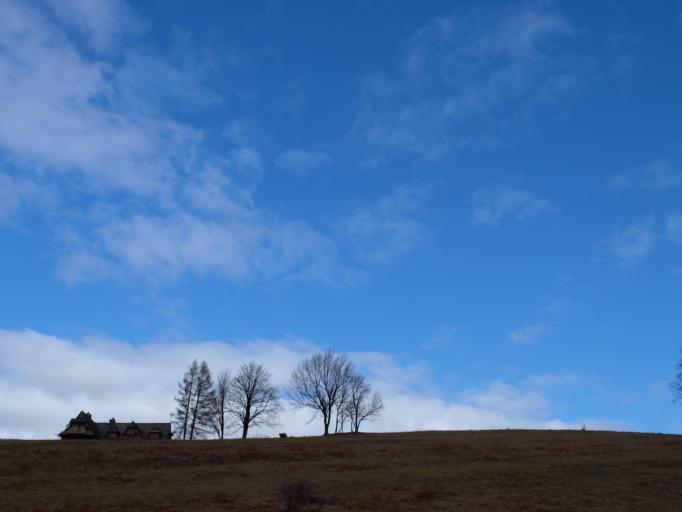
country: PL
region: Lesser Poland Voivodeship
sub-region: Powiat tatrzanski
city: Zakopane
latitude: 49.2940
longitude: 19.9354
